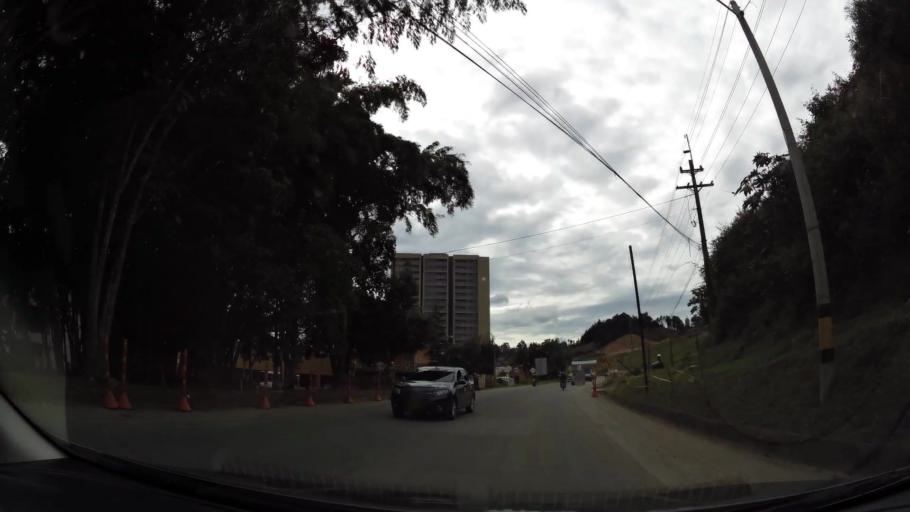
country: CO
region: Antioquia
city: Rionegro
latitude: 6.1509
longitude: -75.3951
